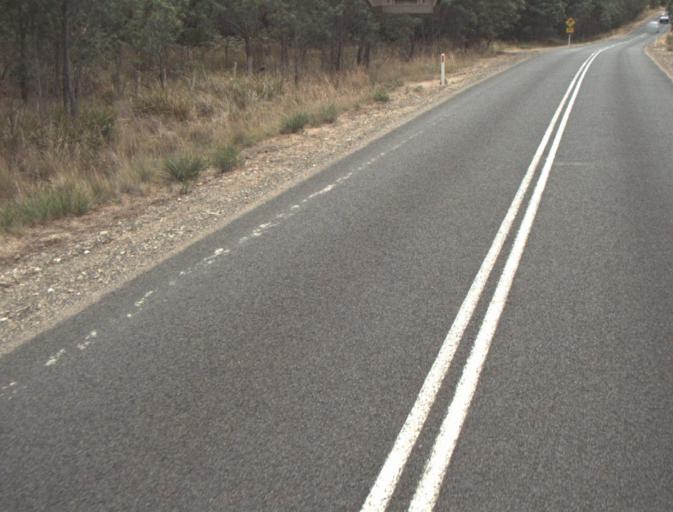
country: AU
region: Tasmania
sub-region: Northern Midlands
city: Evandale
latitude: -41.5084
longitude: 147.3512
